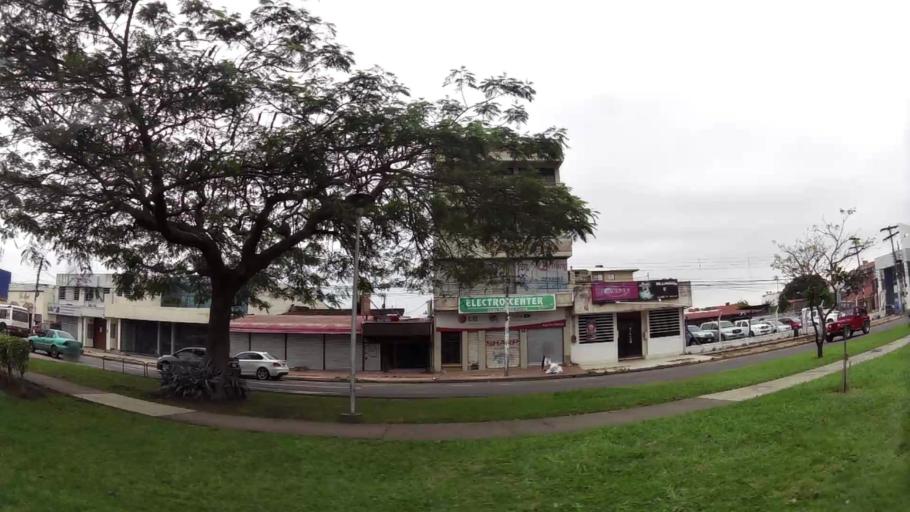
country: BO
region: Santa Cruz
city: Santa Cruz de la Sierra
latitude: -17.7880
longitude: -63.1714
